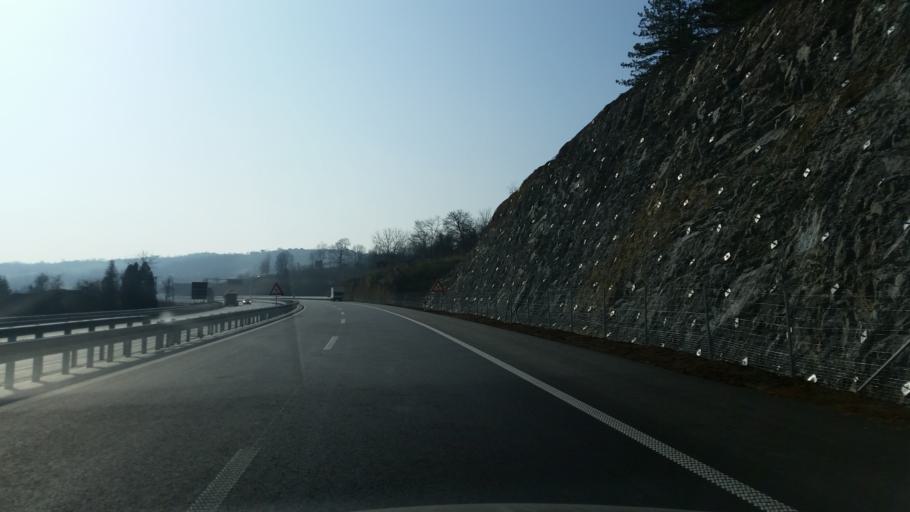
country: RS
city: Prislonica
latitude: 43.9736
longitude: 20.3971
